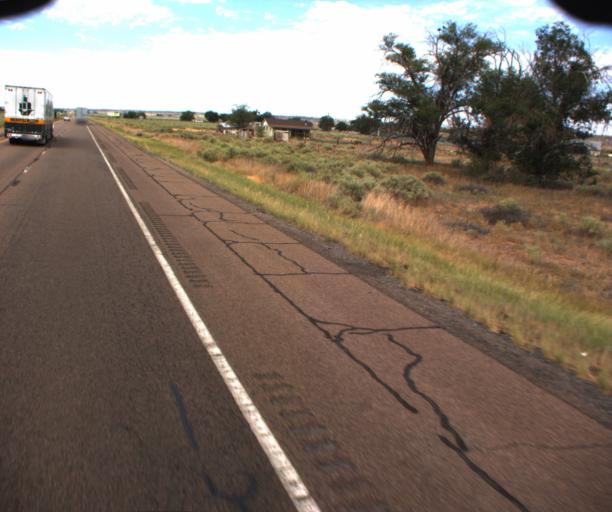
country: US
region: Arizona
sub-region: Apache County
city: Houck
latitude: 35.1981
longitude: -109.4004
